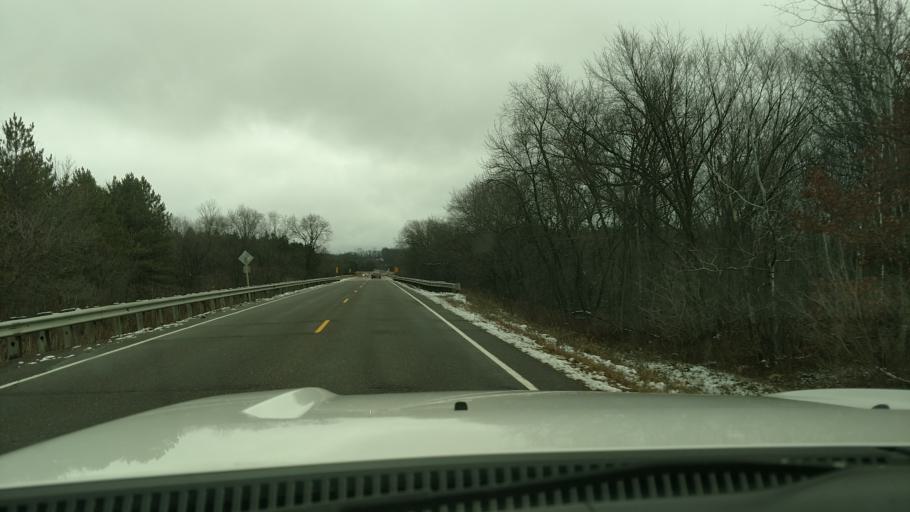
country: US
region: Wisconsin
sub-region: Dunn County
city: Boyceville
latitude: 45.1362
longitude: -91.9393
